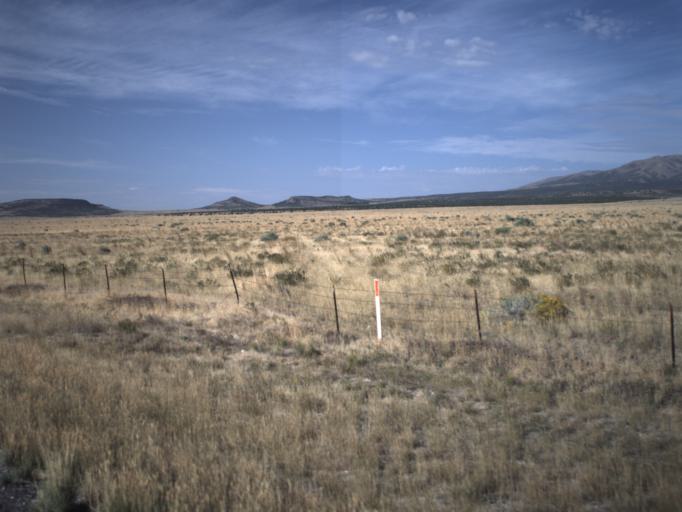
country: US
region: Idaho
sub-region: Oneida County
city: Malad City
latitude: 41.8978
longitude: -113.1080
